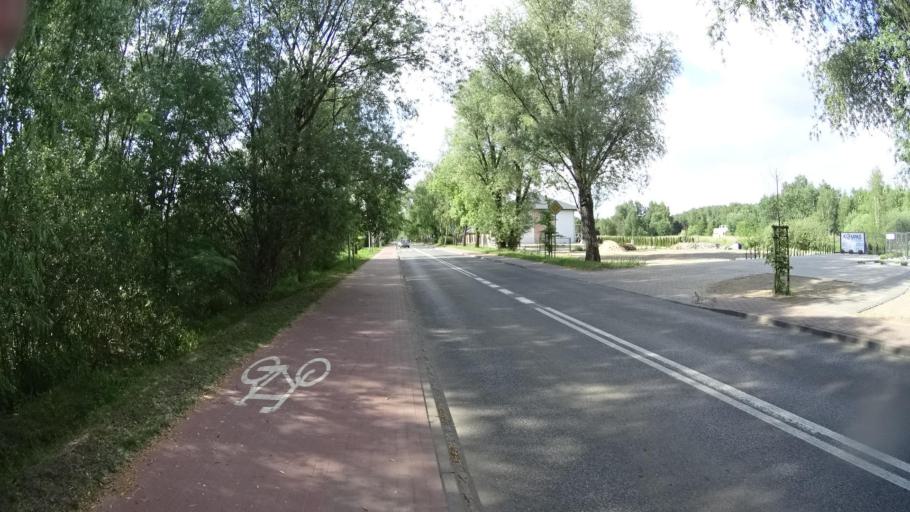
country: PL
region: Masovian Voivodeship
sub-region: Powiat pruszkowski
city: Nadarzyn
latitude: 52.1028
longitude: 20.8038
